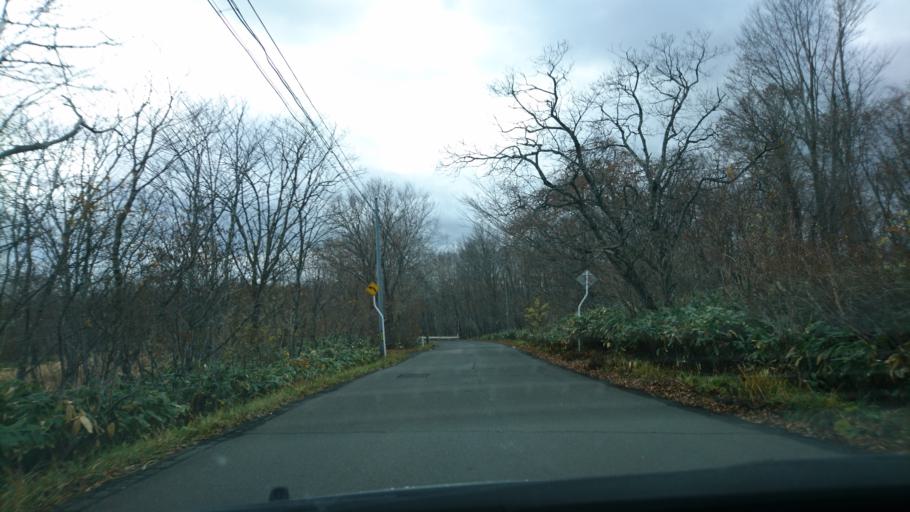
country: JP
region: Iwate
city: Ichinoseki
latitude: 38.9259
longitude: 140.8425
